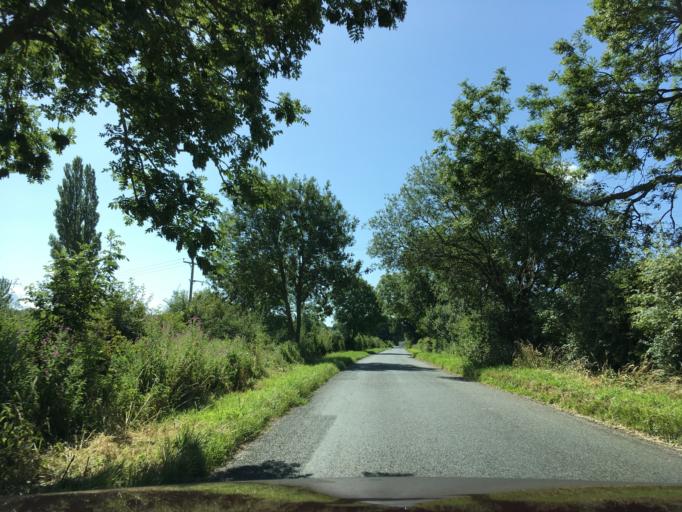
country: GB
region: England
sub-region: Milton Keynes
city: Calverton
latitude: 51.9943
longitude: -0.8607
